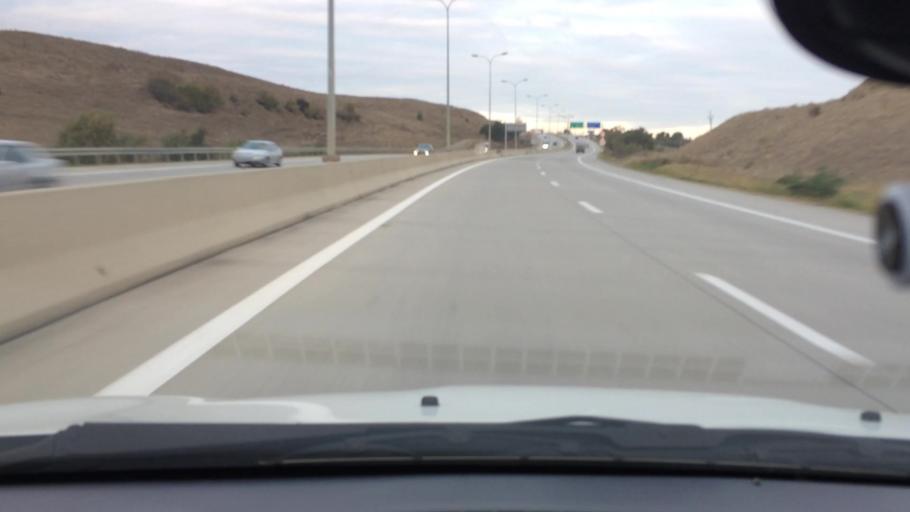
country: GE
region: Shida Kartli
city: Kaspi
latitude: 41.9994
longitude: 44.3925
